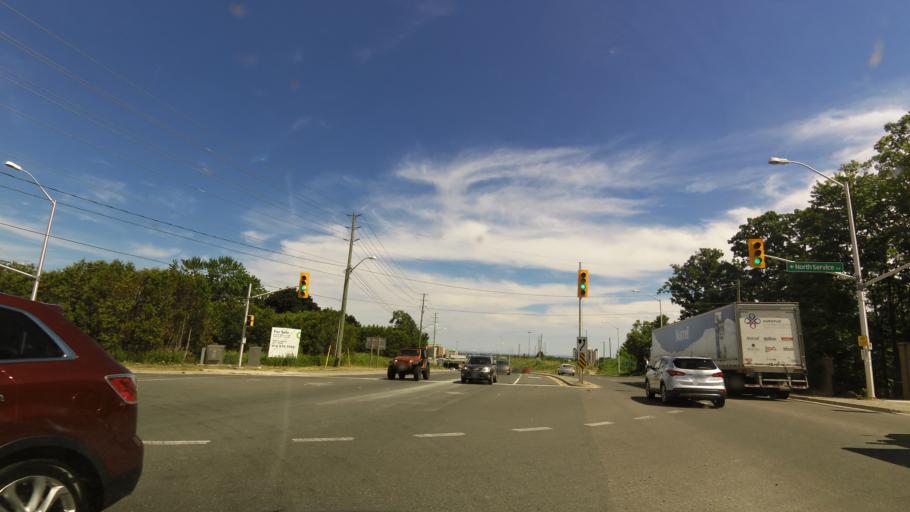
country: CA
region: Ontario
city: Oakville
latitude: 43.4128
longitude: -79.7446
